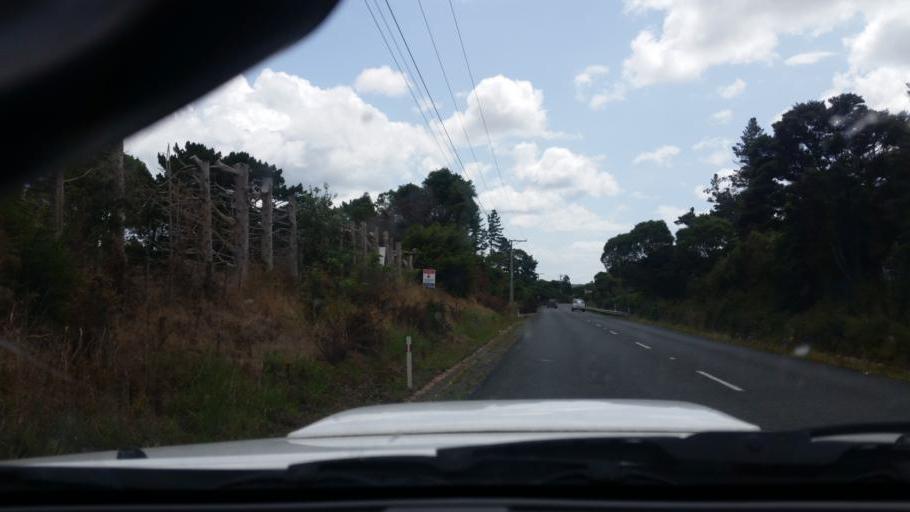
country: NZ
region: Auckland
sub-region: Auckland
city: Wellsford
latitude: -36.1198
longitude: 174.5727
